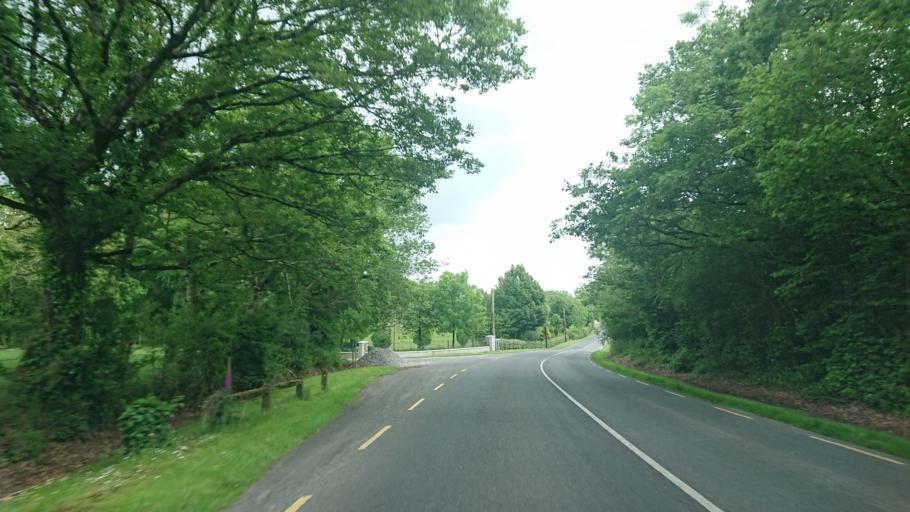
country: IE
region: Leinster
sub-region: Kilkenny
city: Graiguenamanagh
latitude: 52.4817
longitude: -6.9476
